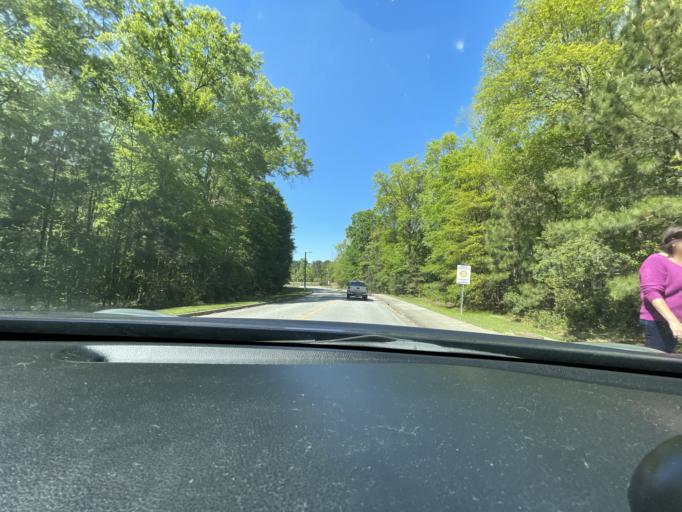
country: US
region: Georgia
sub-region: Chatham County
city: Pooler
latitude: 32.1285
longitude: -81.2610
